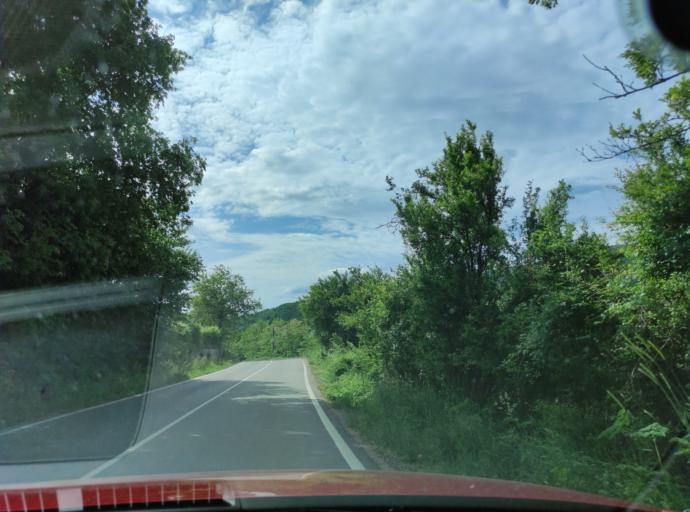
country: BG
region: Montana
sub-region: Obshtina Chiprovtsi
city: Chiprovtsi
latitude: 43.4521
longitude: 22.9073
